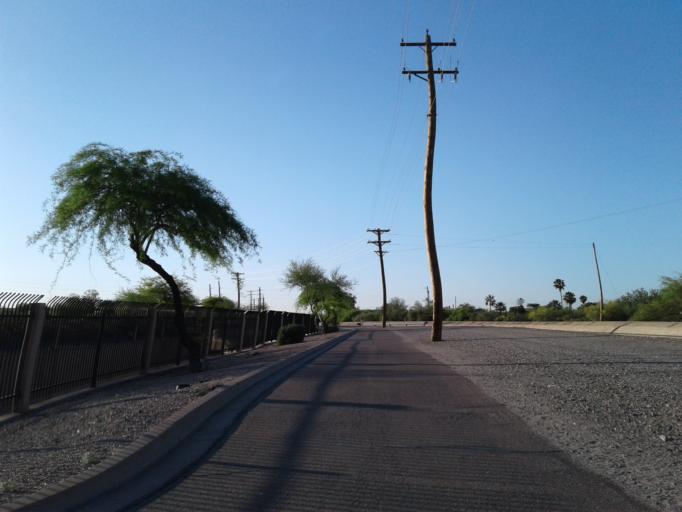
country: US
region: Arizona
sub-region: Maricopa County
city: Phoenix
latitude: 33.5295
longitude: -112.0371
